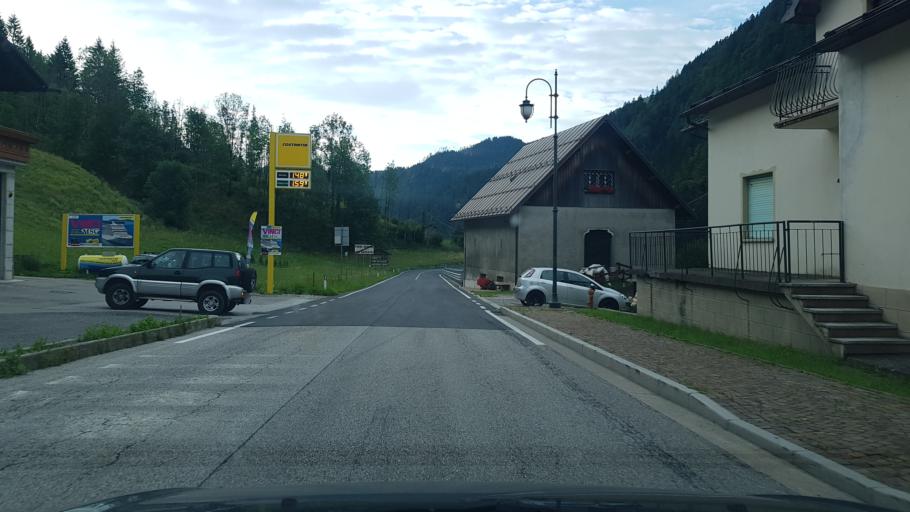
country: IT
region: Friuli Venezia Giulia
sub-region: Provincia di Udine
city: Forni Avoltri
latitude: 46.5839
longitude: 12.7816
